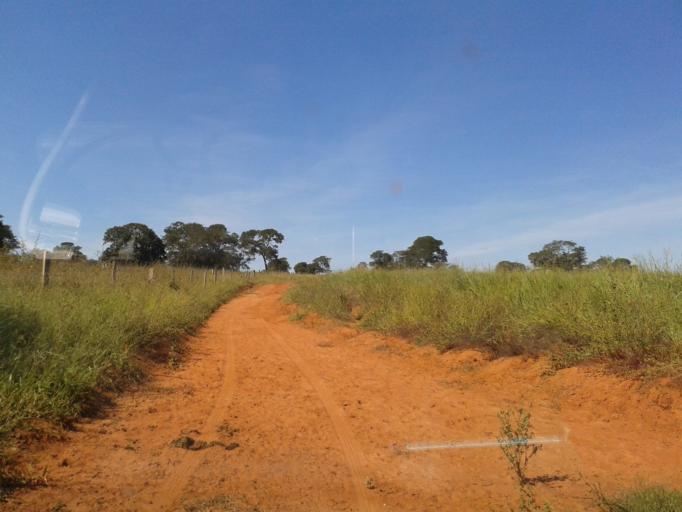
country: BR
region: Minas Gerais
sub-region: Santa Vitoria
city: Santa Vitoria
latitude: -19.0064
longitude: -50.3238
